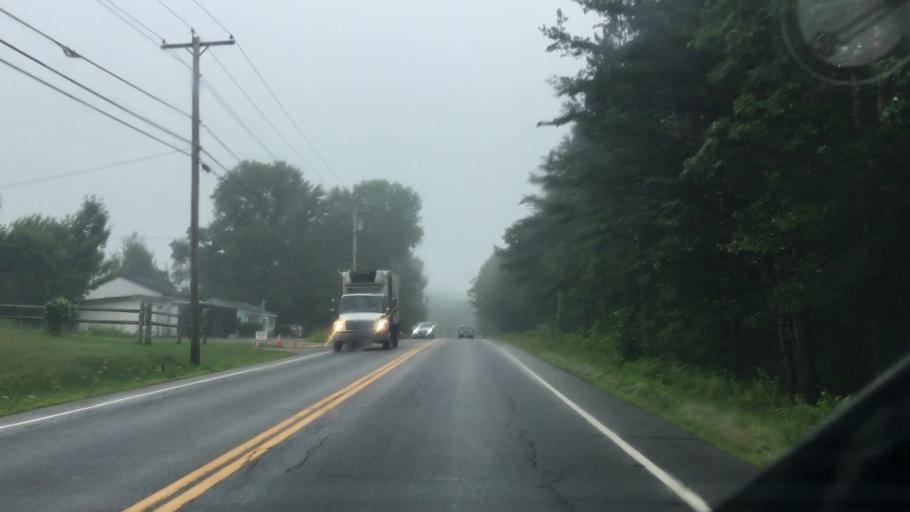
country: US
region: Maine
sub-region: Lincoln County
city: Boothbay
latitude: 43.8908
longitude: -69.6291
